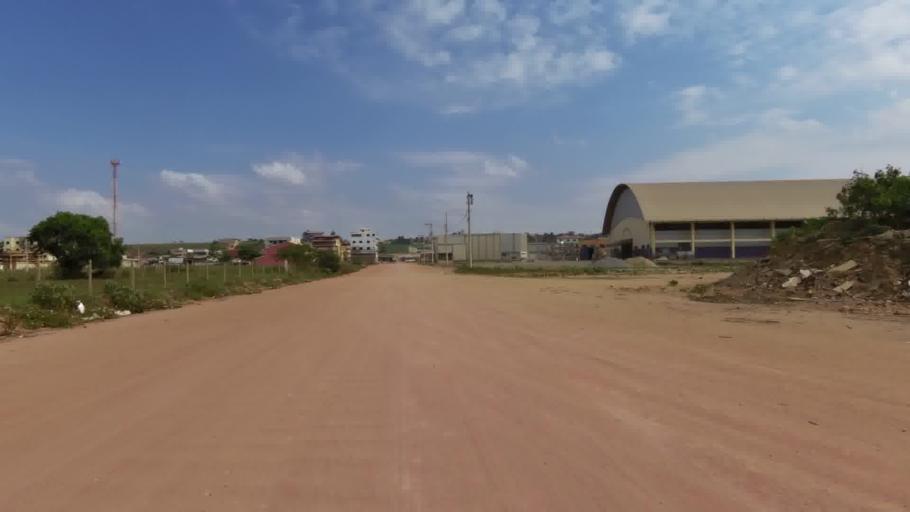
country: BR
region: Espirito Santo
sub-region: Marataizes
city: Marataizes
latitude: -21.0235
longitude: -40.8134
